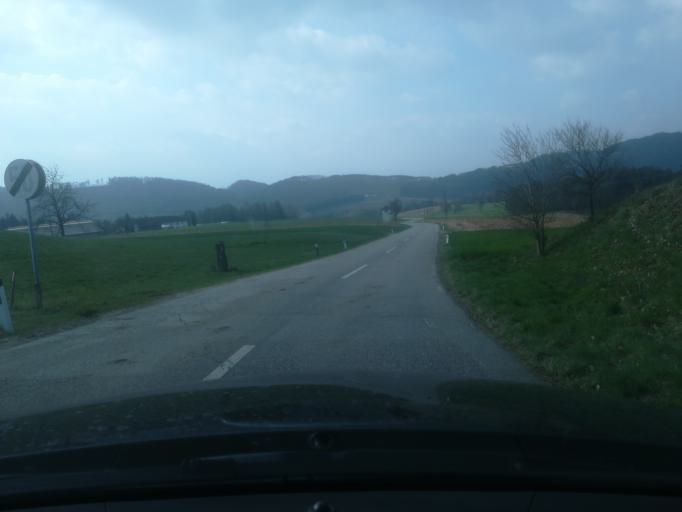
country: AT
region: Upper Austria
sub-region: Politischer Bezirk Perg
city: Perg
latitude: 48.3170
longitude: 14.6233
